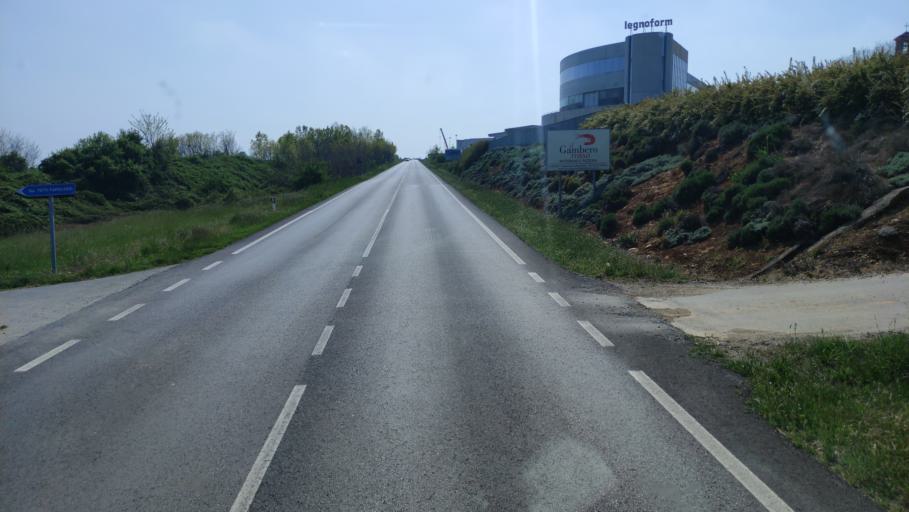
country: IT
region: Piedmont
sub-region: Provincia di Cuneo
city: Marene
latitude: 44.6641
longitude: 7.7504
